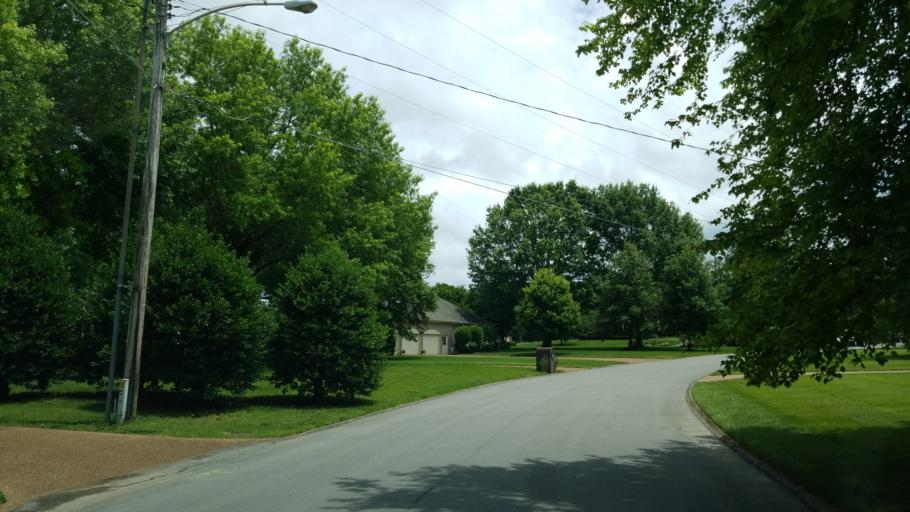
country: US
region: Tennessee
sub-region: Williamson County
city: Brentwood
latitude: 36.0269
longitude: -86.8251
